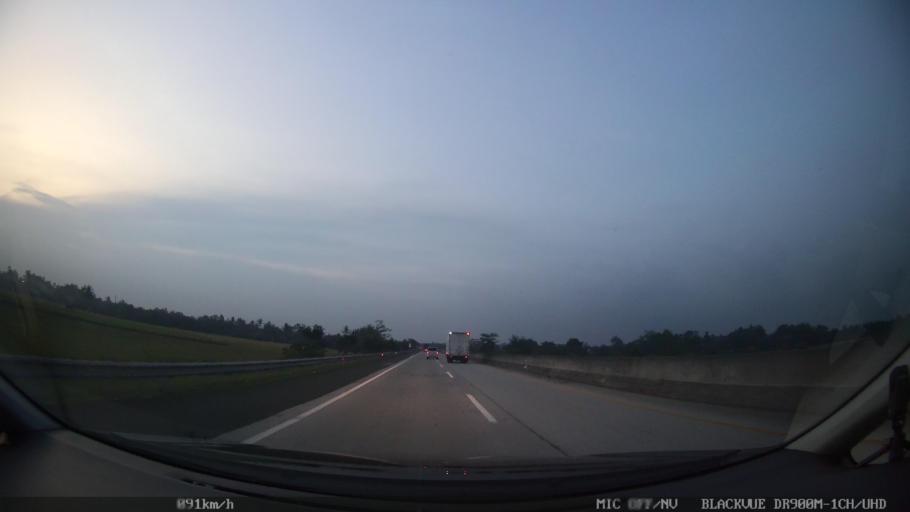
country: ID
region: Lampung
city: Sidorejo
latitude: -5.5760
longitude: 105.5406
